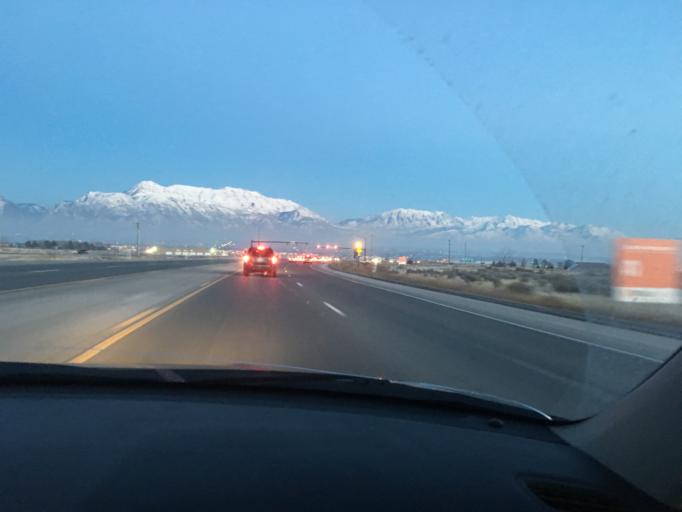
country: US
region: Utah
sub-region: Utah County
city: Saratoga Springs
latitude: 40.3862
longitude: -111.9386
